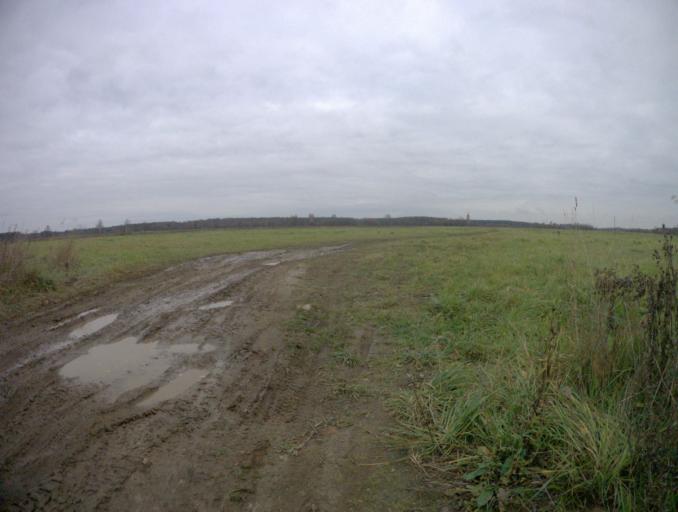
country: RU
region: Moskovskaya
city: Malaya Dubna
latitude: 55.9924
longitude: 38.9775
